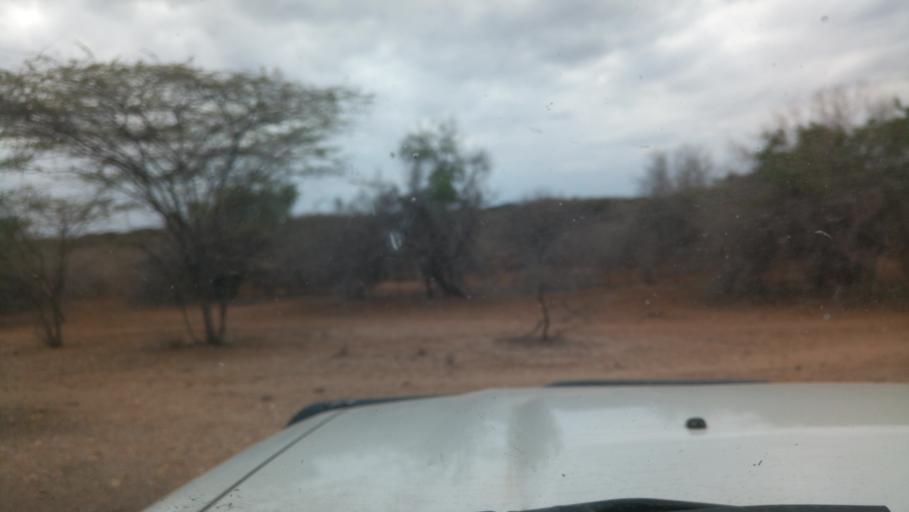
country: KE
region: Garissa
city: Garissa
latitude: -0.1167
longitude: 38.9531
